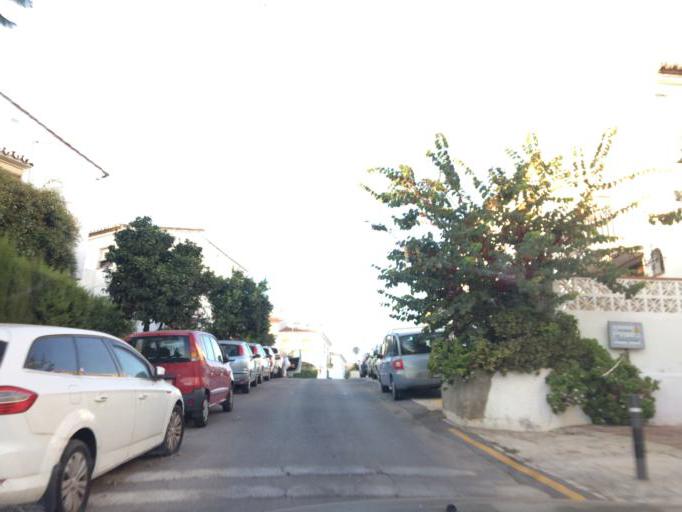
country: ES
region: Andalusia
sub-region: Provincia de Malaga
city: Rincon de la Victoria
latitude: 36.7203
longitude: -4.2967
